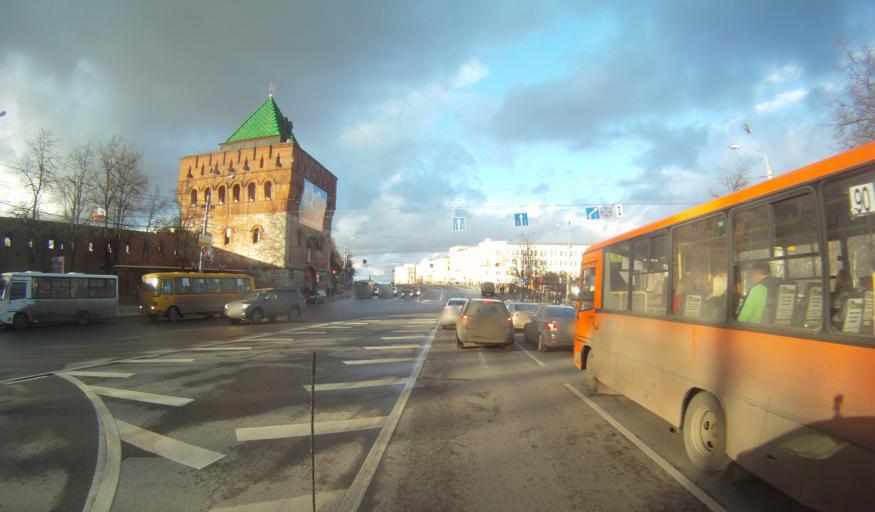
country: RU
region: Nizjnij Novgorod
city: Nizhniy Novgorod
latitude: 56.3265
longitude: 44.0052
